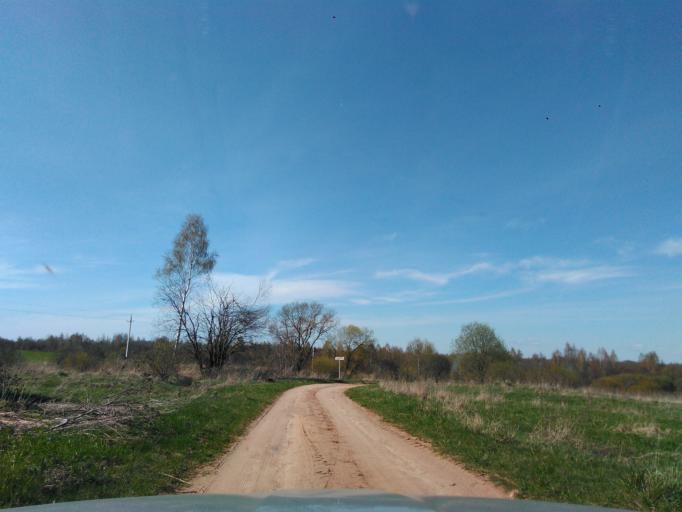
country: BY
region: Vitebsk
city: Konstantinovo
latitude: 54.6779
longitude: 29.4791
